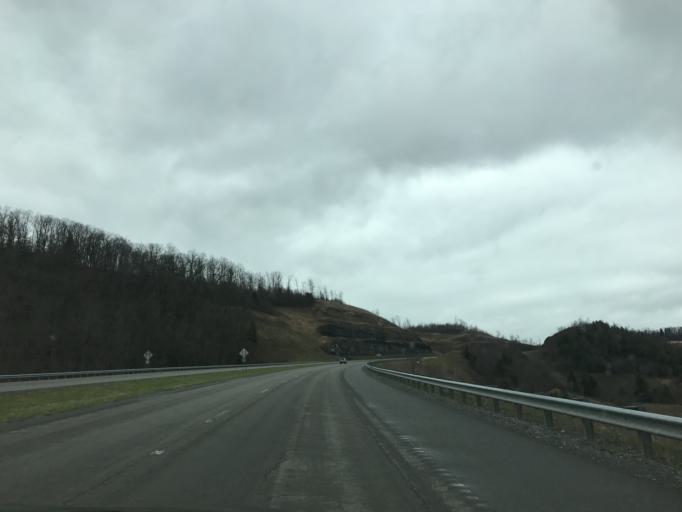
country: US
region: West Virginia
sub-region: Raleigh County
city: Sophia
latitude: 37.7059
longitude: -81.3053
